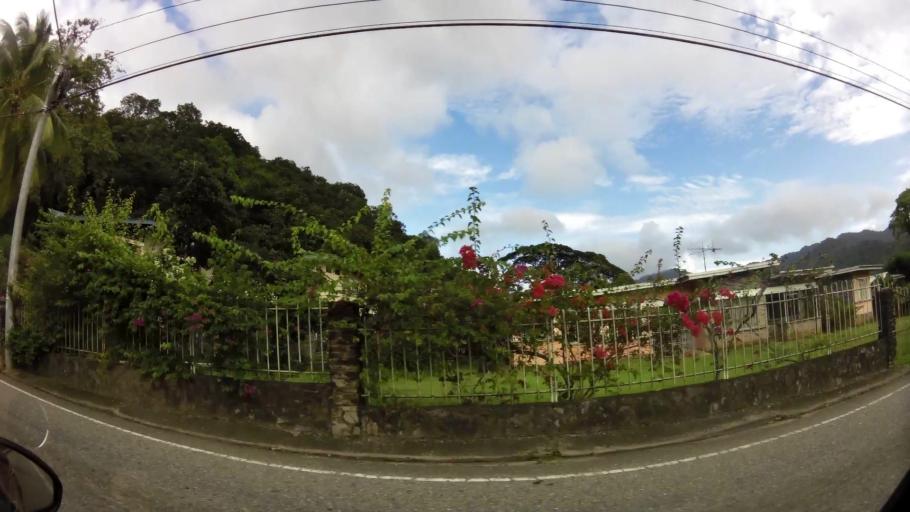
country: TT
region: Diego Martin
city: Petit Valley
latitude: 10.7165
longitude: -61.4728
